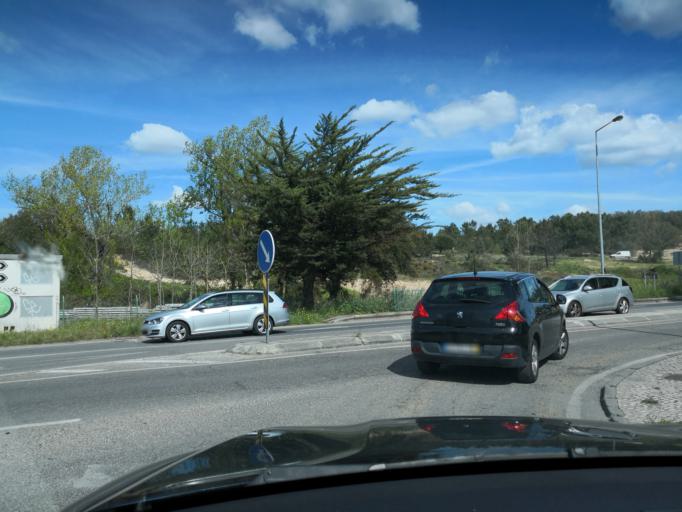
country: PT
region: Setubal
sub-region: Barreiro
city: Santo Antonio da Charneca
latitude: 38.5543
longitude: -9.0349
